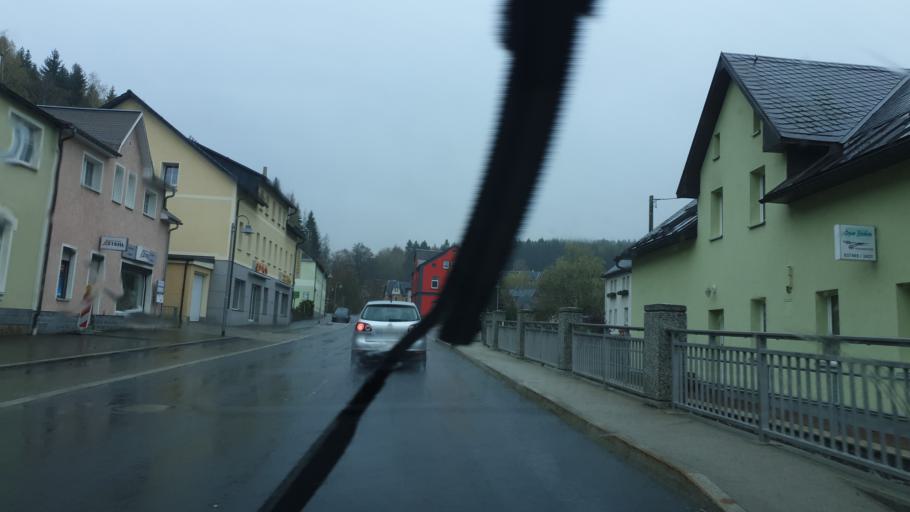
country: DE
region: Saxony
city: Tannenbergsthal
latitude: 50.4368
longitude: 12.4615
